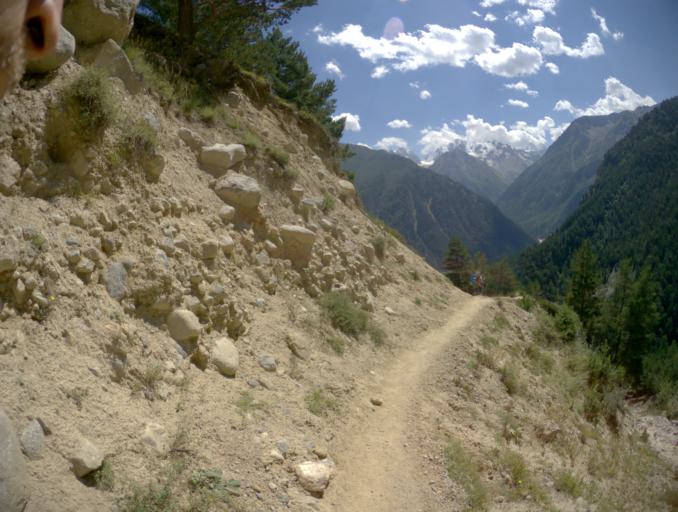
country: RU
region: Kabardino-Balkariya
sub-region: El'brusskiy Rayon
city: El'brus
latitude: 43.2672
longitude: 42.6339
